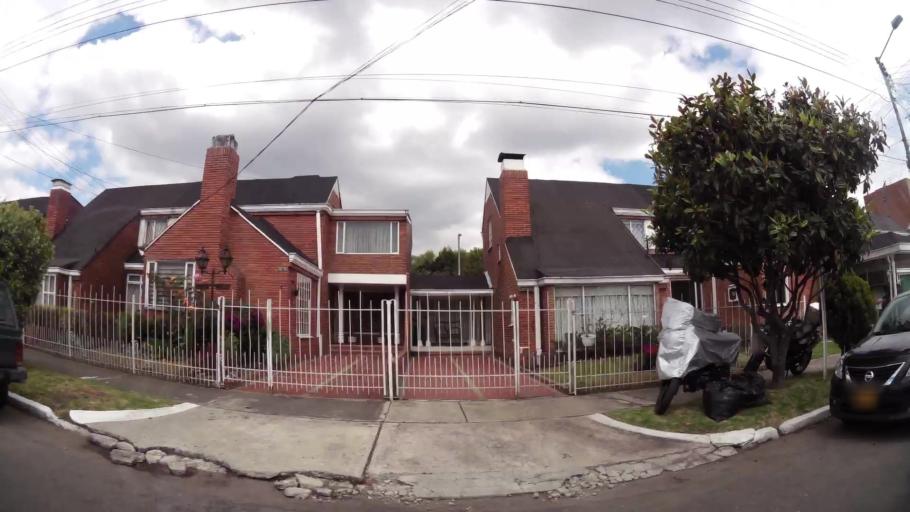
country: CO
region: Bogota D.C.
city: Barrio San Luis
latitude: 4.7061
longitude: -74.0644
